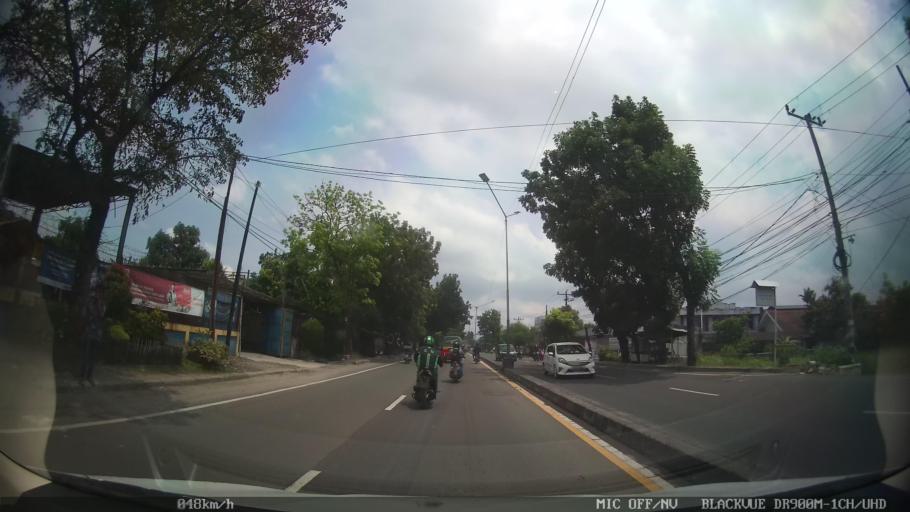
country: ID
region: North Sumatra
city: Medan
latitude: 3.6397
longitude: 98.6639
